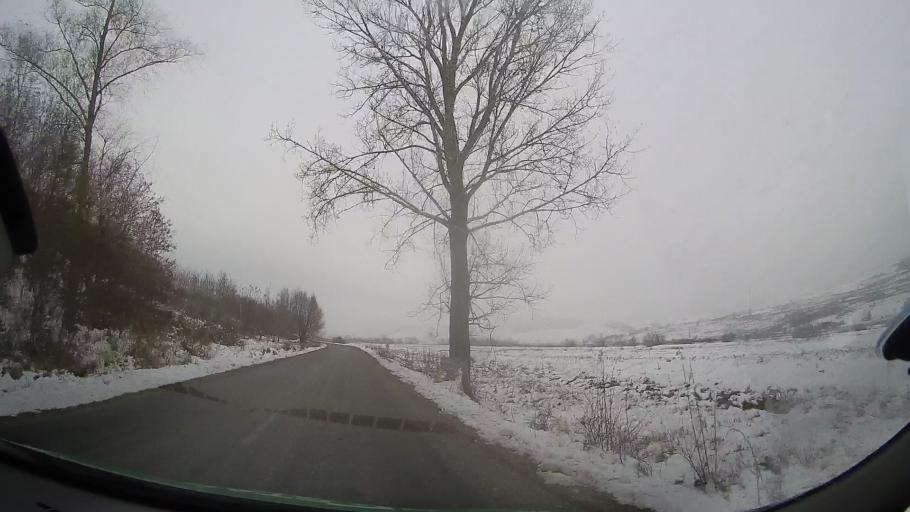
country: RO
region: Bacau
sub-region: Comuna Vultureni
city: Vultureni
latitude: 46.3102
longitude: 27.2926
